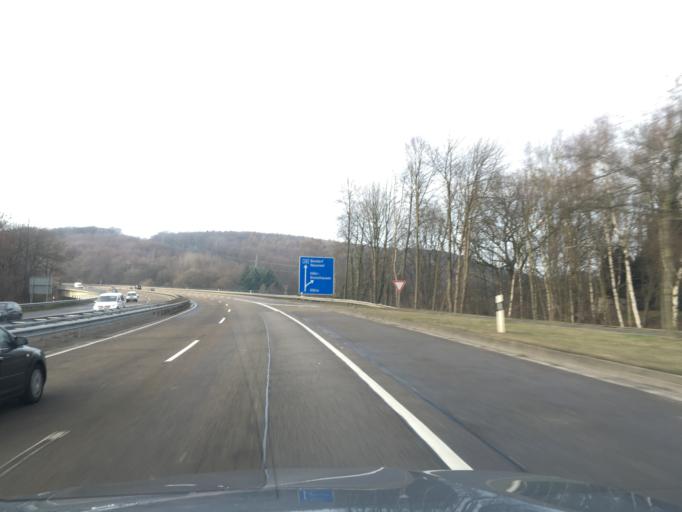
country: DE
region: Rheinland-Pfalz
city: Hilgert
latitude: 50.4474
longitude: 7.6785
